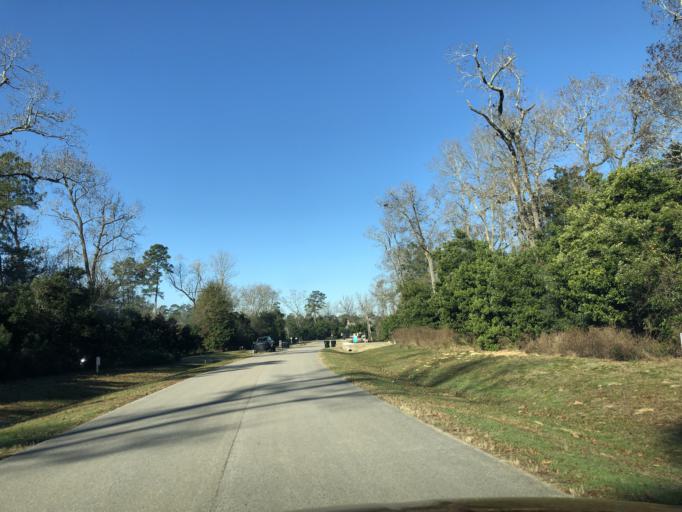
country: US
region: Texas
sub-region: Montgomery County
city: Porter Heights
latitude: 30.0709
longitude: -95.3325
